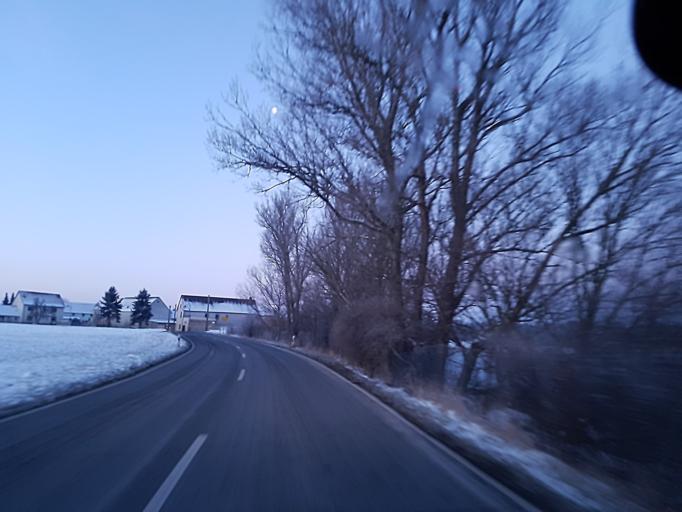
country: DE
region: Brandenburg
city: Muhlberg
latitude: 51.4223
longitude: 13.1827
